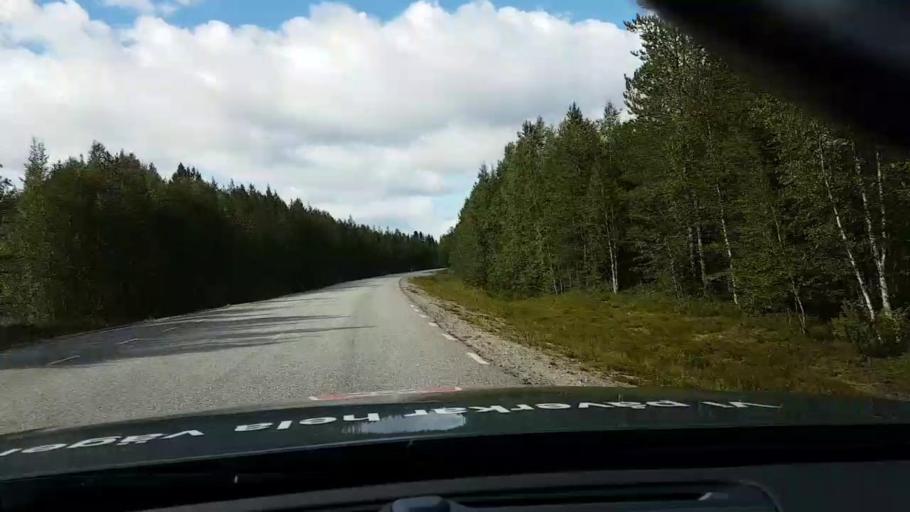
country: SE
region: Vaesterbotten
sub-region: Asele Kommun
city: Asele
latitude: 63.9309
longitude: 17.2973
